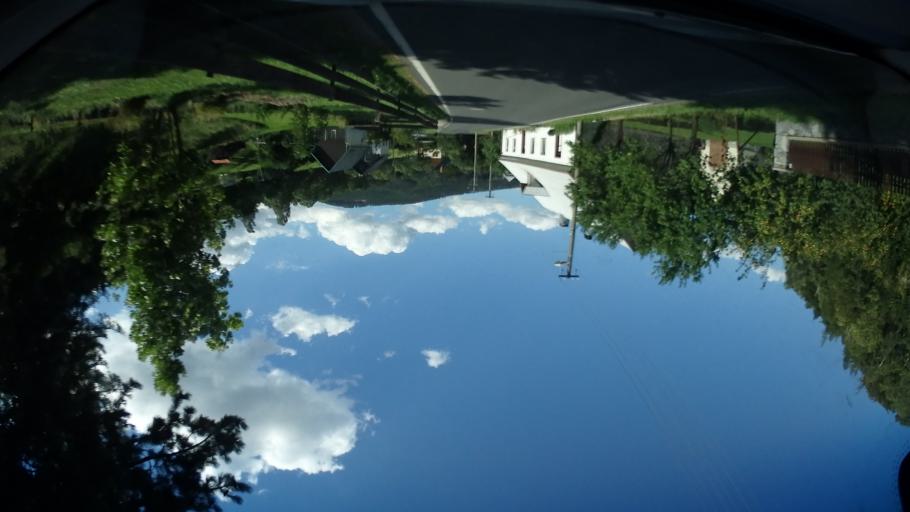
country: CZ
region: Olomoucky
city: Vapenna
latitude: 50.2232
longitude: 17.0975
